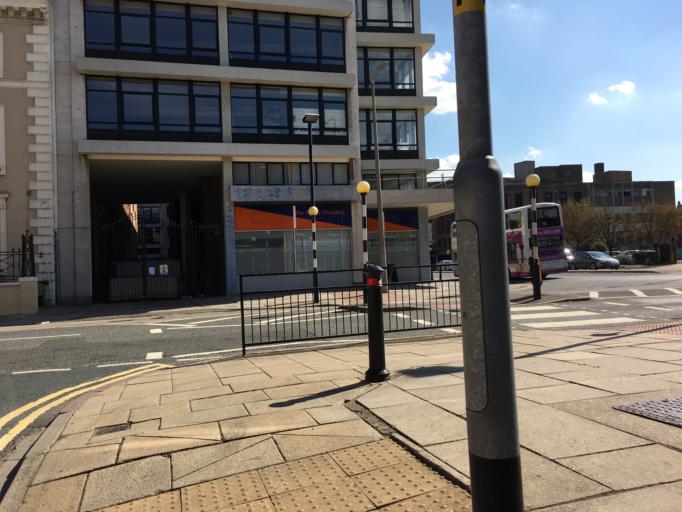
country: GB
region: England
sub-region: City of Kingston upon Hull
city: Hull
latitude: 53.7471
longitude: -0.3394
